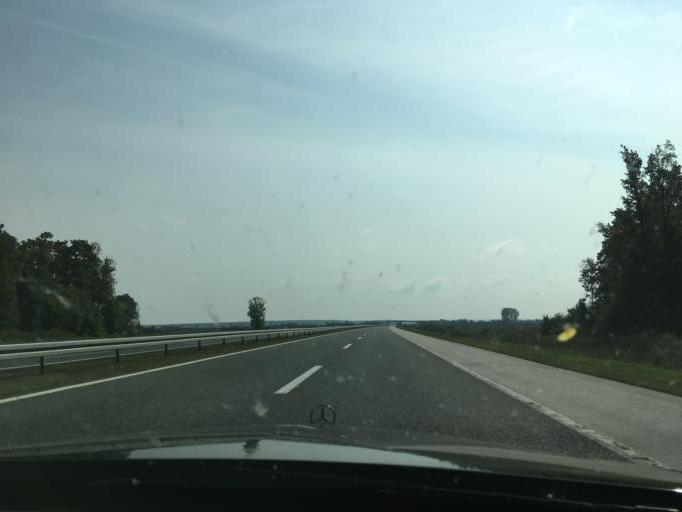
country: HR
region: Vukovarsko-Srijemska
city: Bosnjaci
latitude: 45.0872
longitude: 18.7584
